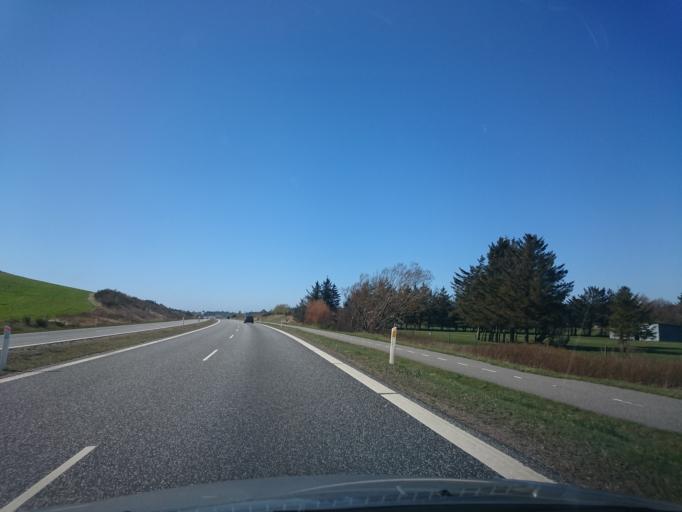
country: DK
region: North Denmark
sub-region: Hjorring Kommune
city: Hirtshals
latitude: 57.5708
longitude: 10.0074
